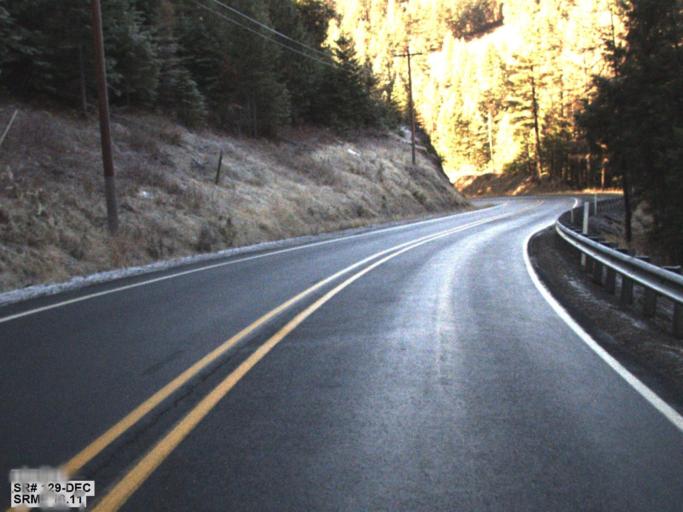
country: US
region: Washington
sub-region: Asotin County
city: Asotin
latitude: 46.0876
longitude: -117.1757
